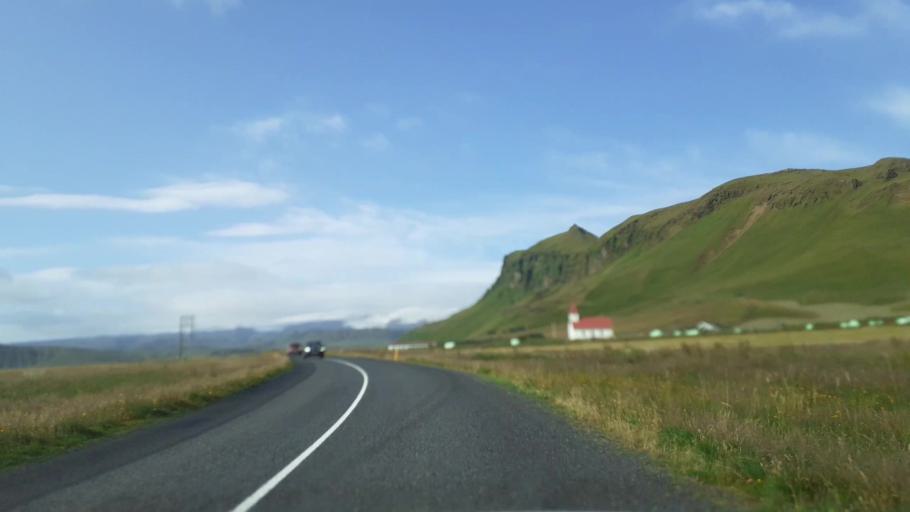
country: IS
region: South
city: Vestmannaeyjar
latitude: 63.4168
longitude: -19.0480
